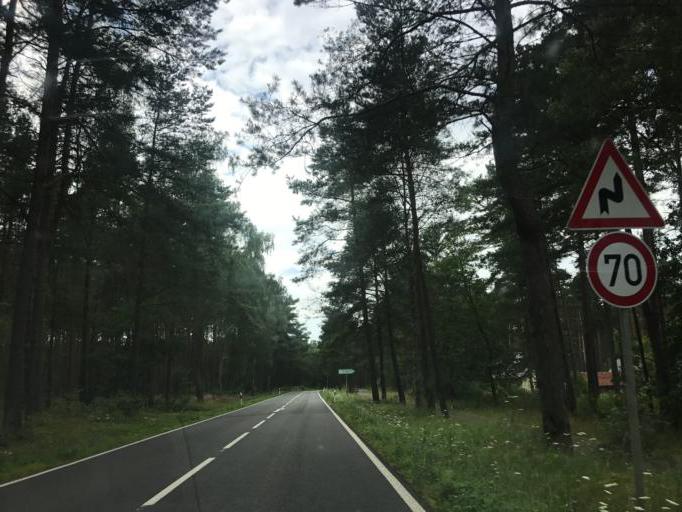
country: DE
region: Brandenburg
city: Rheinsberg
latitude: 53.1020
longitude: 12.9357
